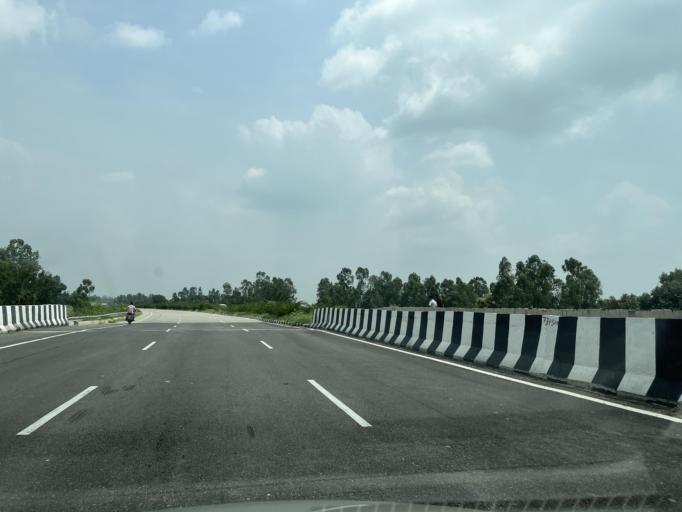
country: IN
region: Uttar Pradesh
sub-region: Bijnor
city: Nagina
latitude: 29.4314
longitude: 78.4055
